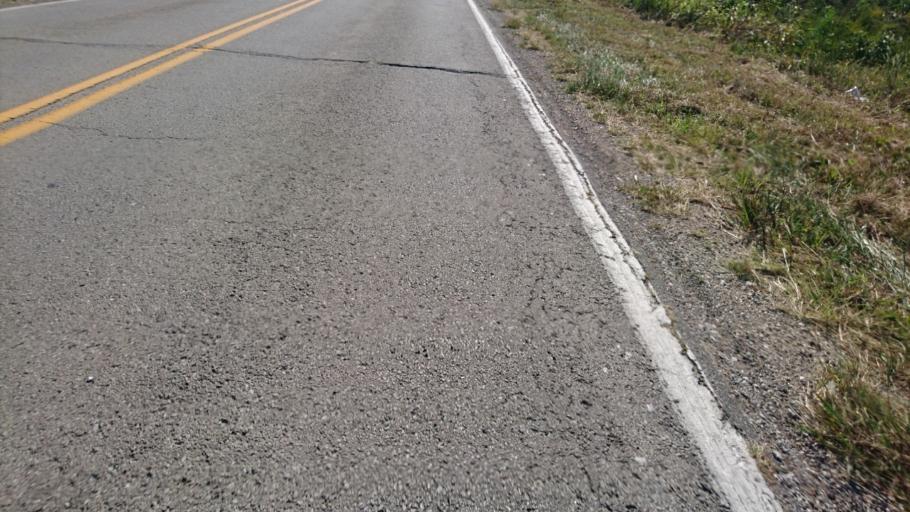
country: US
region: Missouri
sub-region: Laclede County
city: Lebanon
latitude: 37.6415
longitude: -92.6744
